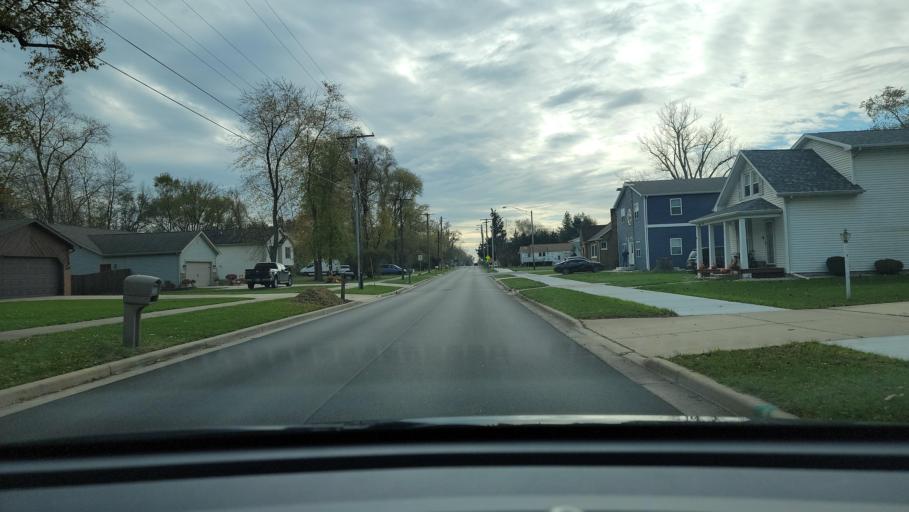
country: US
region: Indiana
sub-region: Porter County
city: Portage
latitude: 41.5819
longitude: -87.1439
